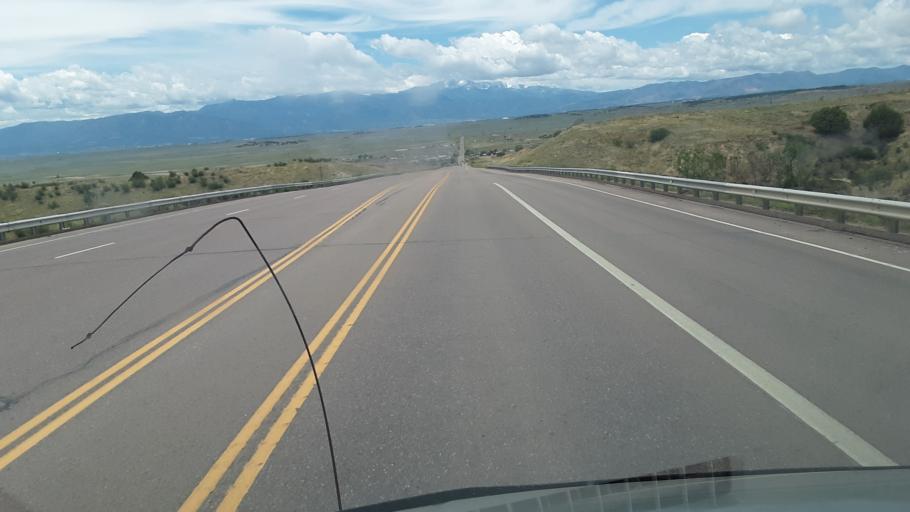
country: US
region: Colorado
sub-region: El Paso County
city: Cimarron Hills
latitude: 38.8385
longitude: -104.5743
